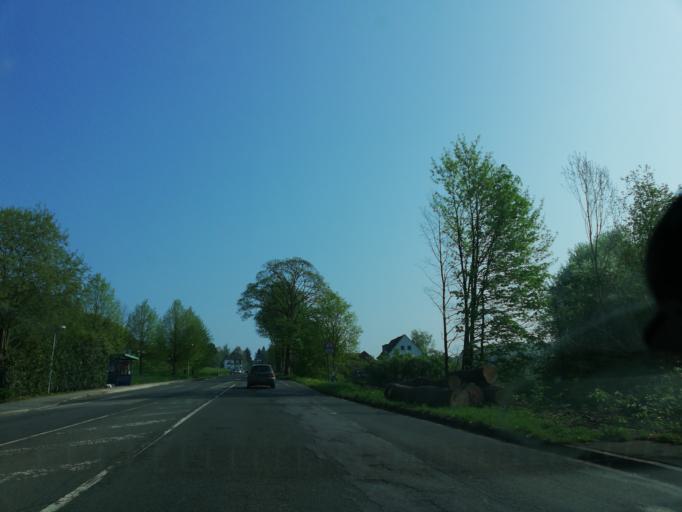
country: DE
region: North Rhine-Westphalia
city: Herdecke
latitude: 51.4269
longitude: 7.4421
